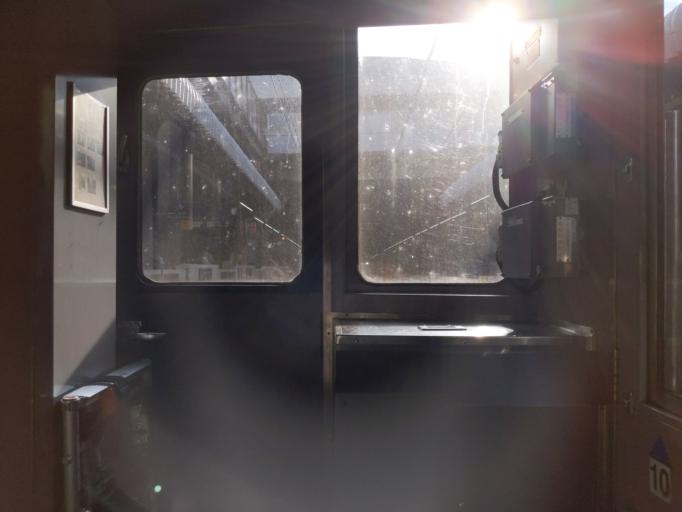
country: JP
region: Tokyo
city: Tokyo
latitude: 35.6484
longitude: 139.7039
